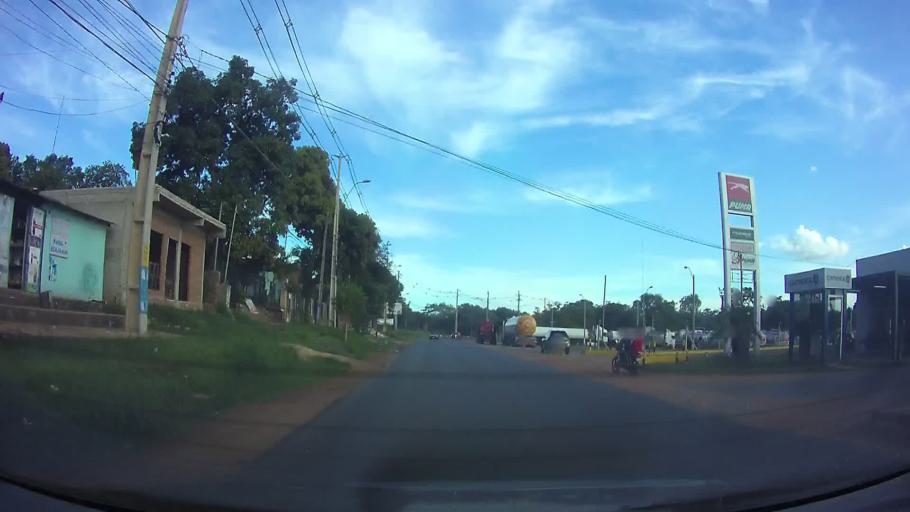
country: PY
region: Central
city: San Antonio
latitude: -25.4303
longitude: -57.5539
